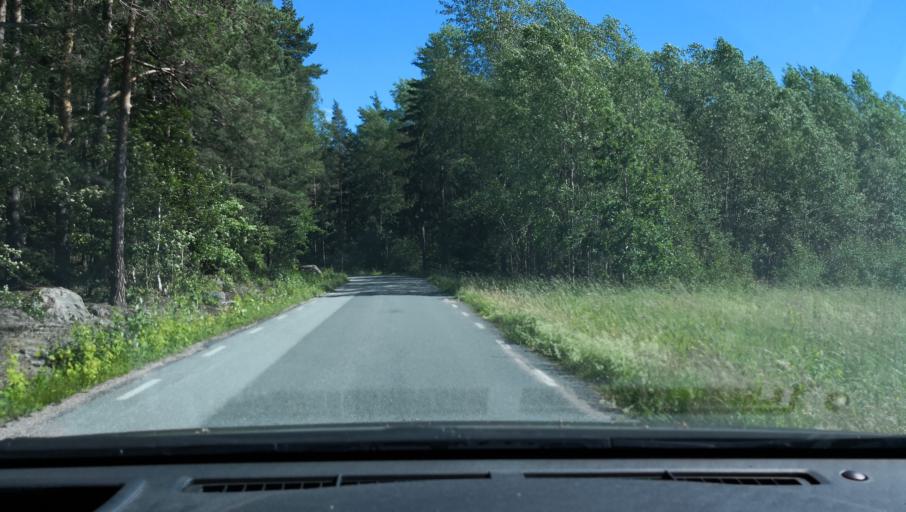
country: SE
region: Soedermanland
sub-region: Eskilstuna Kommun
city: Hallbybrunn
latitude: 59.3053
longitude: 16.3701
